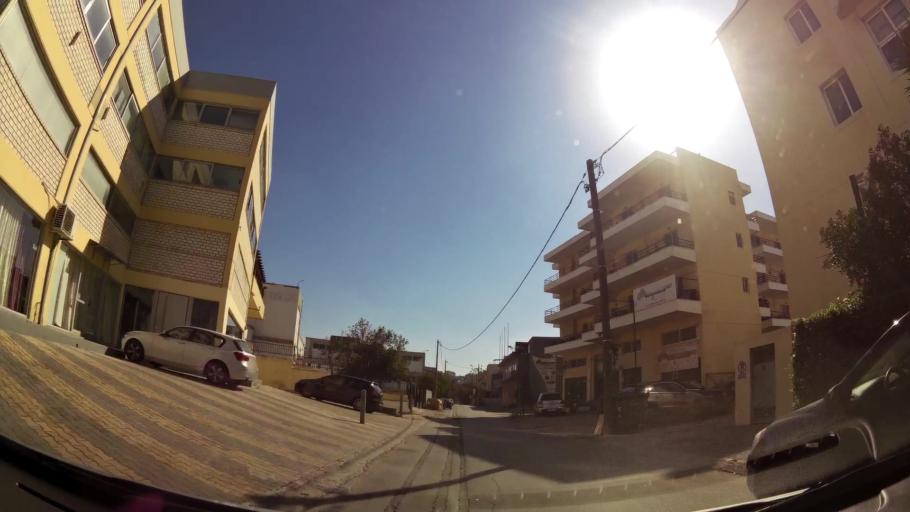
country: GR
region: Attica
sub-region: Nomarchia Athinas
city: Metamorfosi
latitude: 38.0695
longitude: 23.7632
